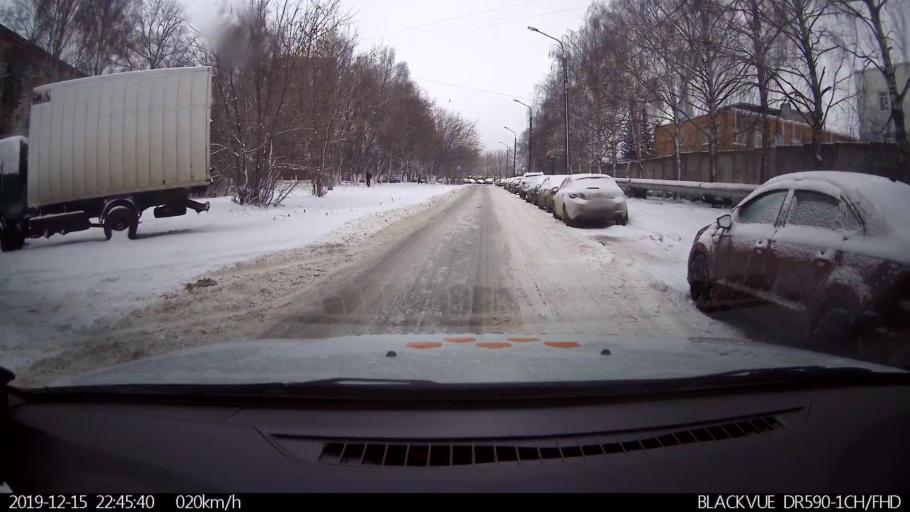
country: RU
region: Nizjnij Novgorod
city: Nizhniy Novgorod
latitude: 56.2409
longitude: 43.9722
